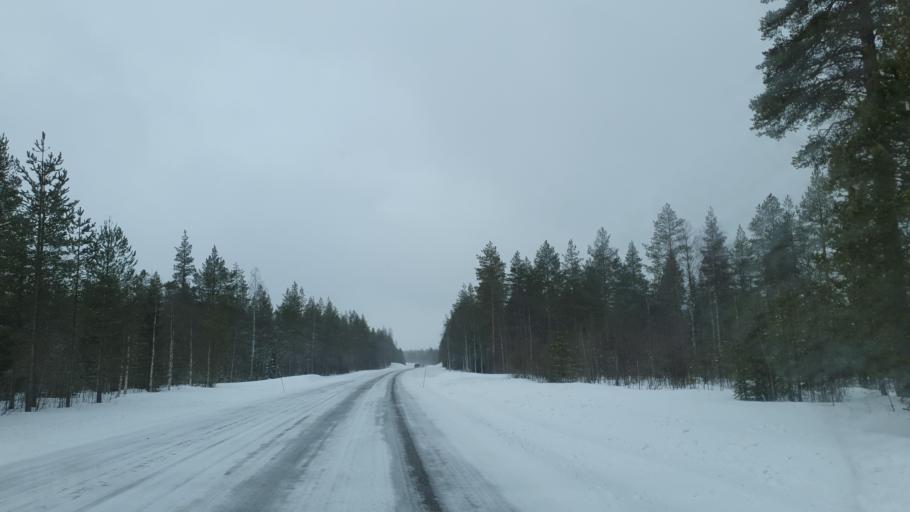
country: FI
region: Lapland
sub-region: Rovaniemi
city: Ranua
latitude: 66.0344
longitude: 26.3343
